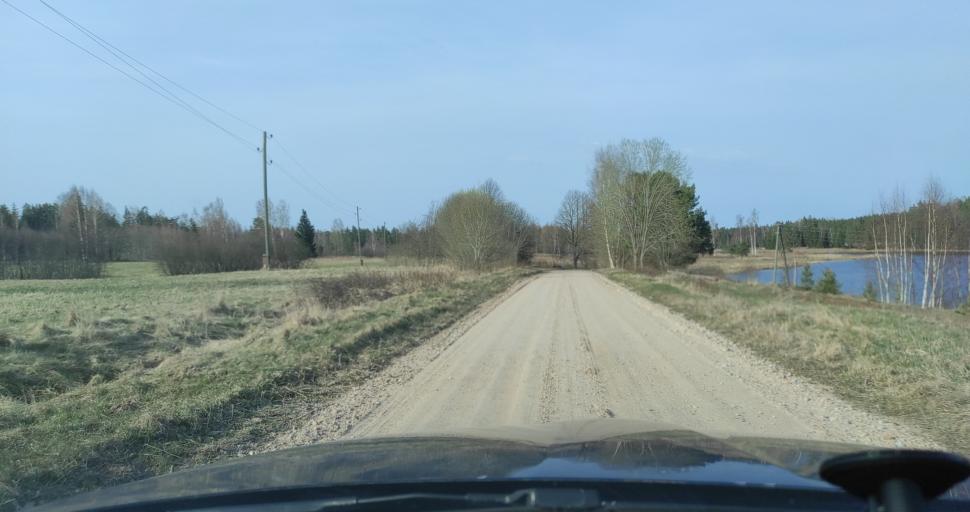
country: LV
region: Kuldigas Rajons
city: Kuldiga
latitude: 57.0066
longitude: 22.0148
